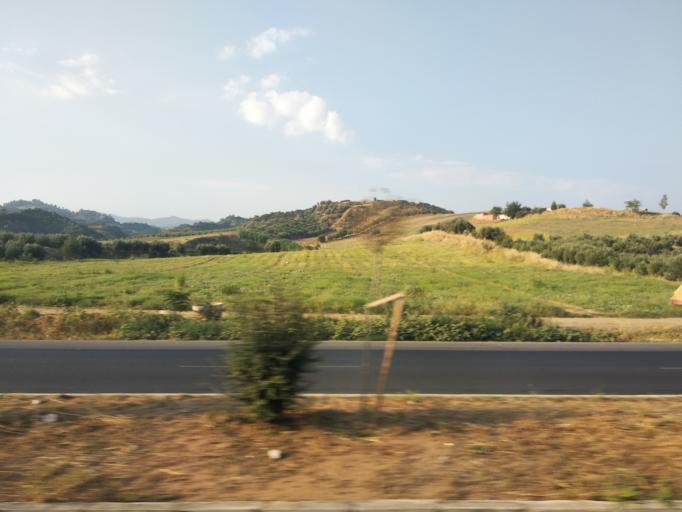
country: TR
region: Manisa
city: Ahmetli
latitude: 38.5089
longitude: 27.9827
